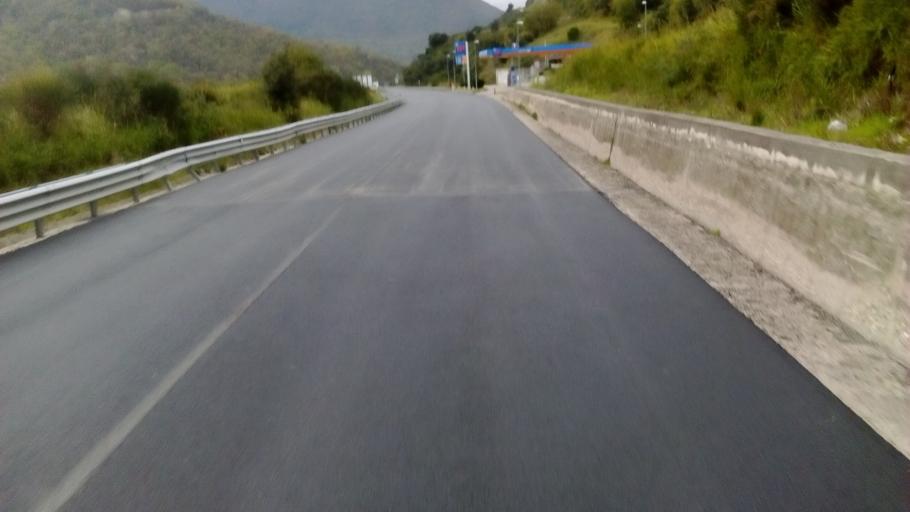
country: IT
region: Molise
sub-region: Provincia di Campobasso
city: Montemitro
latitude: 41.9195
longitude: 14.6625
